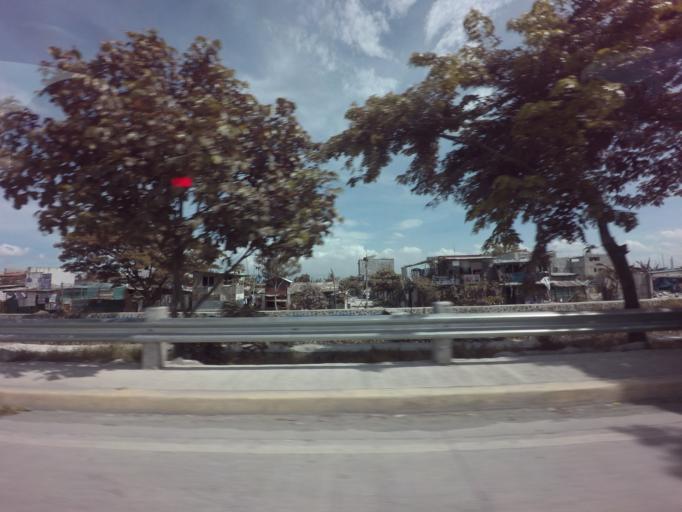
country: PH
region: Calabarzon
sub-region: Province of Rizal
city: Taguig
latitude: 14.5325
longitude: 121.0982
